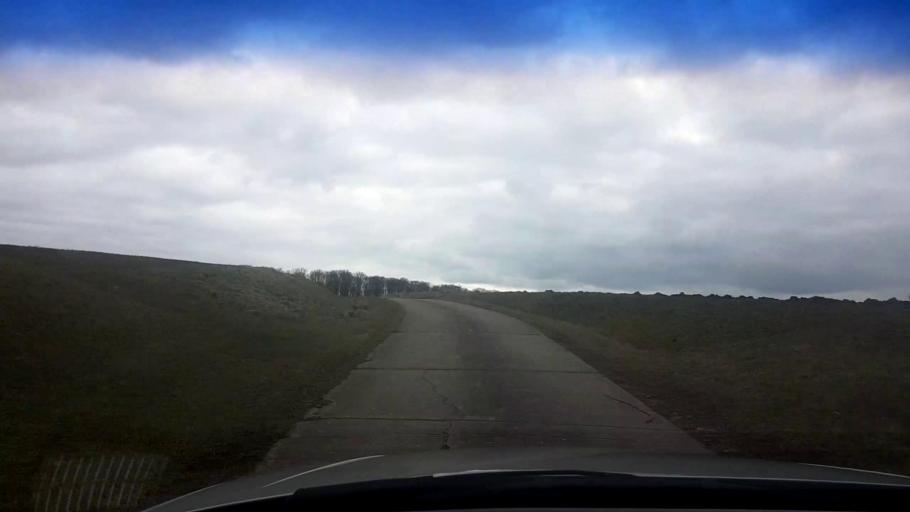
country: DE
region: Bavaria
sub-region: Regierungsbezirk Unterfranken
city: Stettfeld
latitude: 49.9391
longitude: 10.7139
